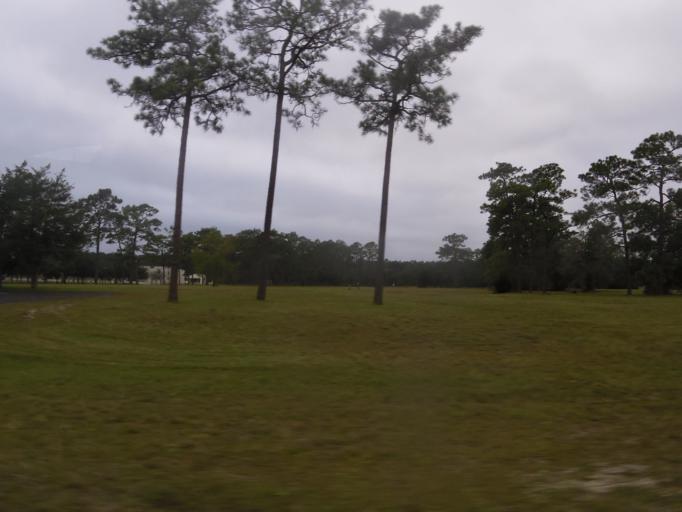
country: US
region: Florida
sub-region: Duval County
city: Baldwin
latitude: 30.2263
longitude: -81.8873
